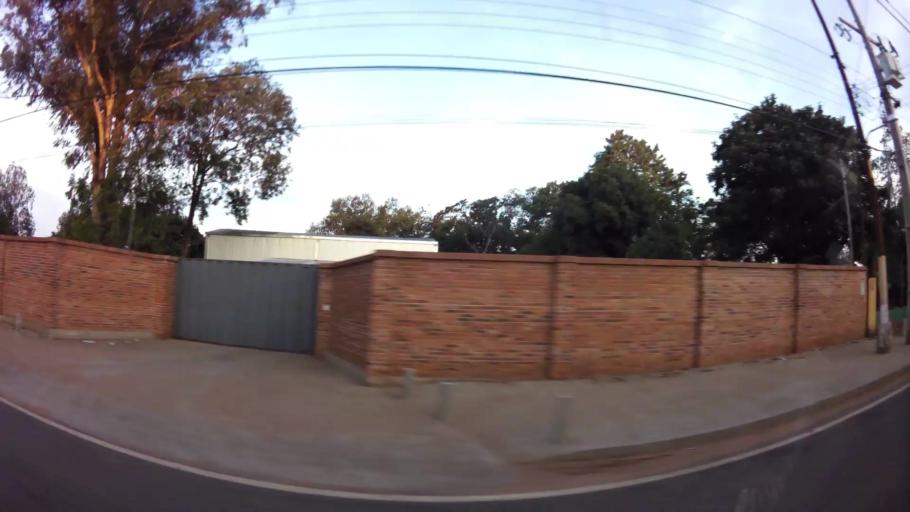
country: PY
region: Central
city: San Lorenzo
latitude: -25.3676
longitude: -57.4911
